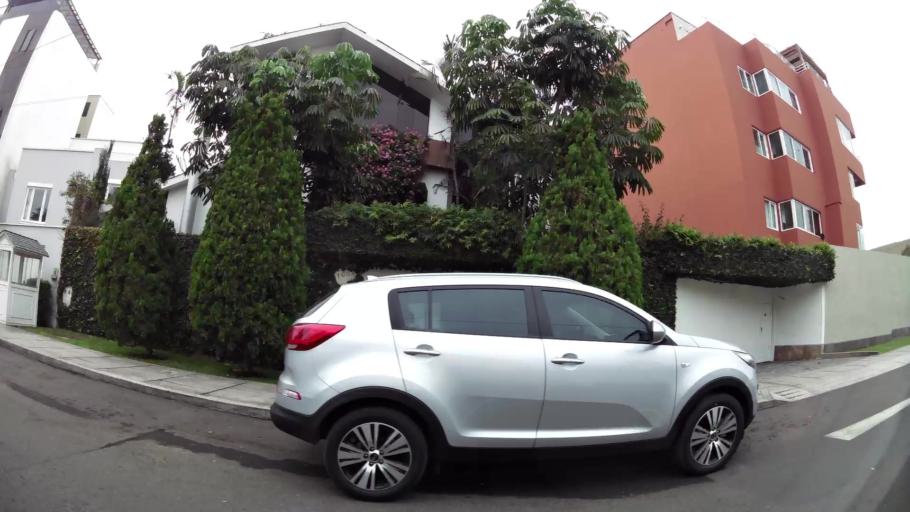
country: PE
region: Lima
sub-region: Lima
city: San Isidro
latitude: -12.0978
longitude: -77.0416
